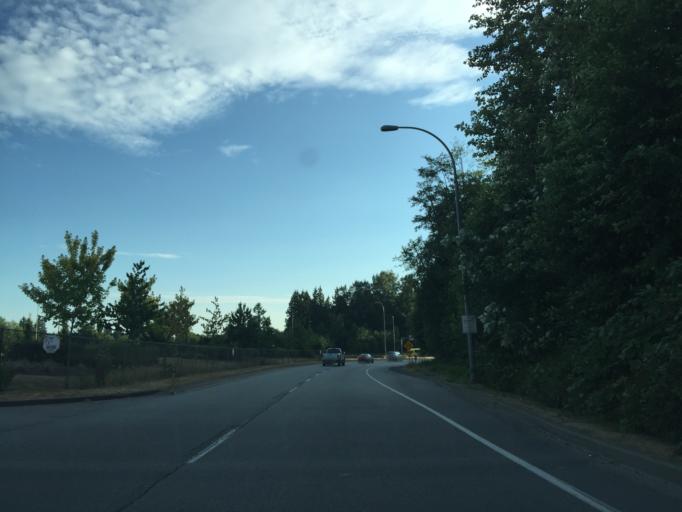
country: CA
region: British Columbia
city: Walnut Grove
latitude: 49.1660
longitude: -122.6704
